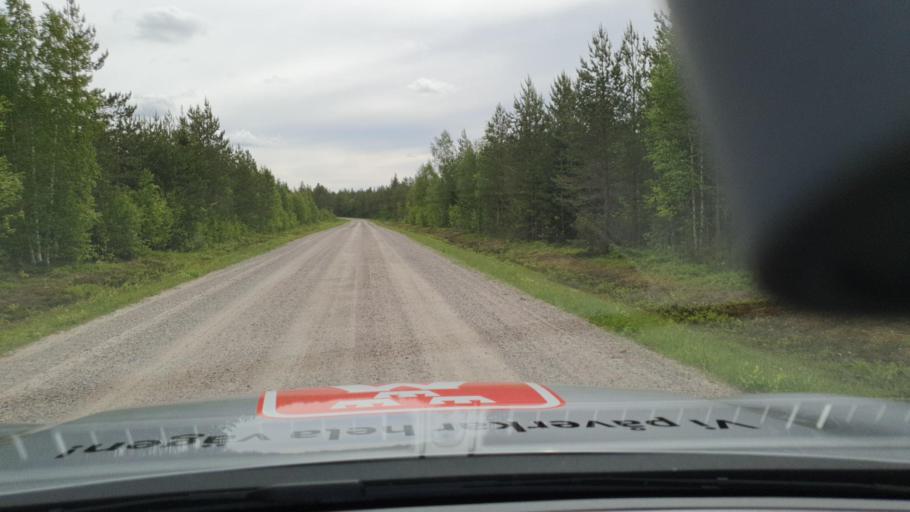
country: FI
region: Lapland
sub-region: Torniolaakso
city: Ylitornio
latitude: 65.9529
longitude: 23.7637
